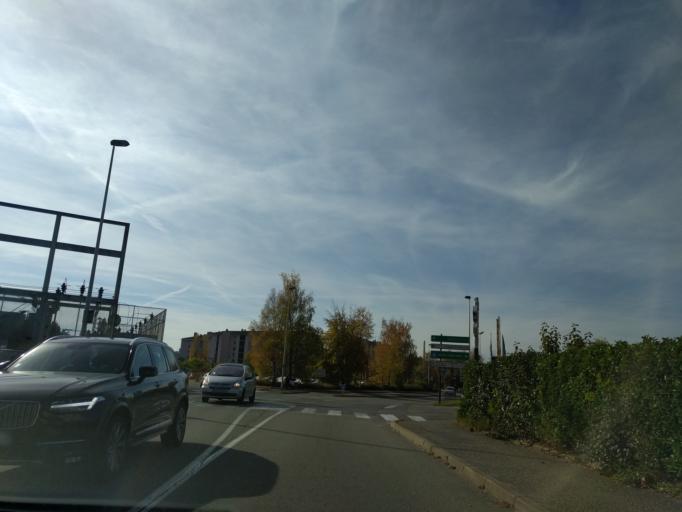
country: FR
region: Rhone-Alpes
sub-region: Departement de la Haute-Savoie
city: Annecy-le-Vieux
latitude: 45.9245
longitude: 6.1276
